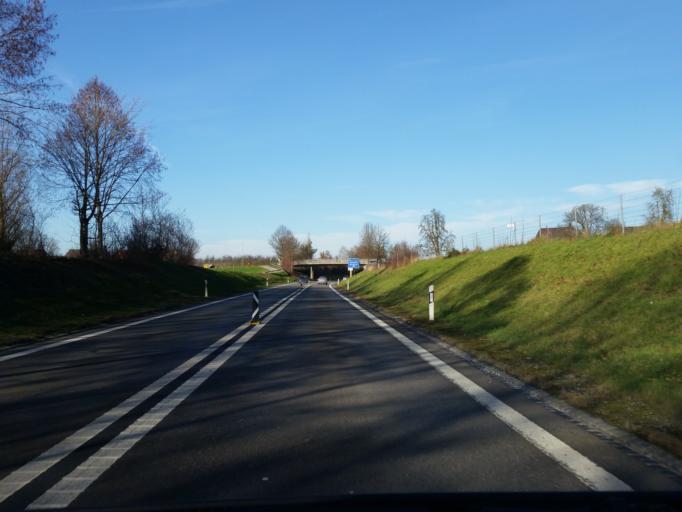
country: CH
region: Thurgau
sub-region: Arbon District
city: Roggwil
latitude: 47.5181
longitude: 9.4017
